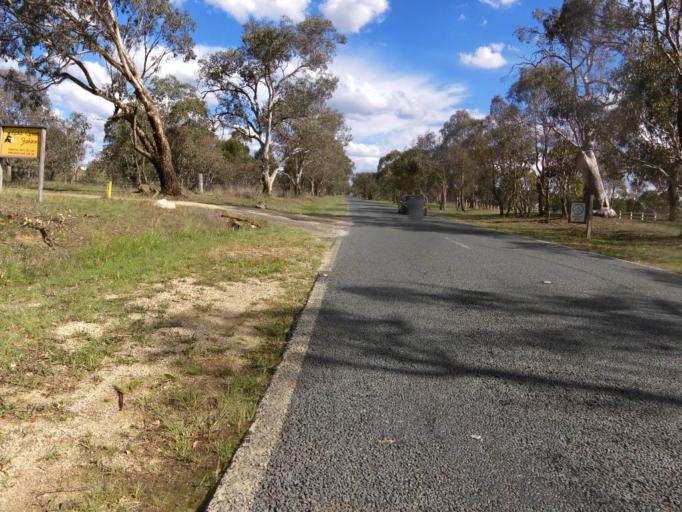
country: AU
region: Australian Capital Territory
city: Belconnen
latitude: -35.1773
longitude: 149.0722
